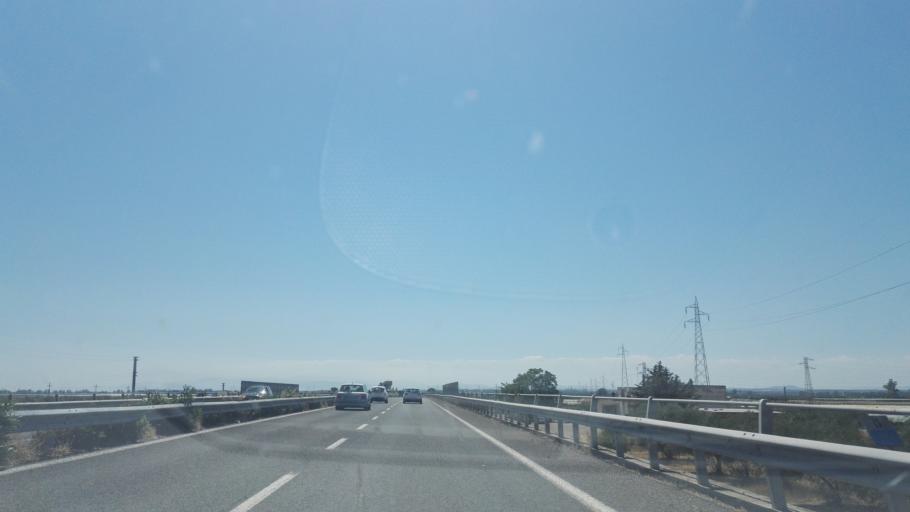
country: IT
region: Apulia
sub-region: Provincia di Taranto
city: Marina di Ginosa
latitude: 40.4432
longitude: 16.8497
